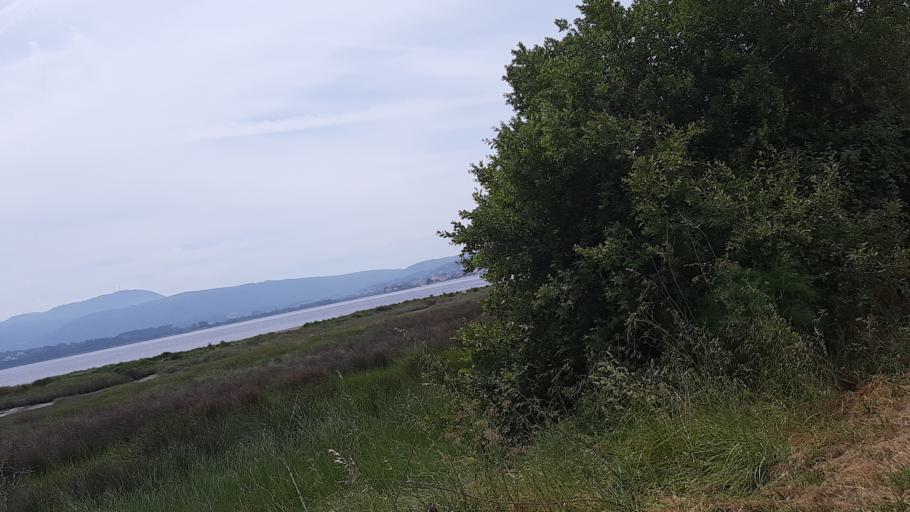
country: ES
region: Galicia
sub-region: Provincia de Pontevedra
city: A Guarda
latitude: 41.8961
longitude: -8.8494
